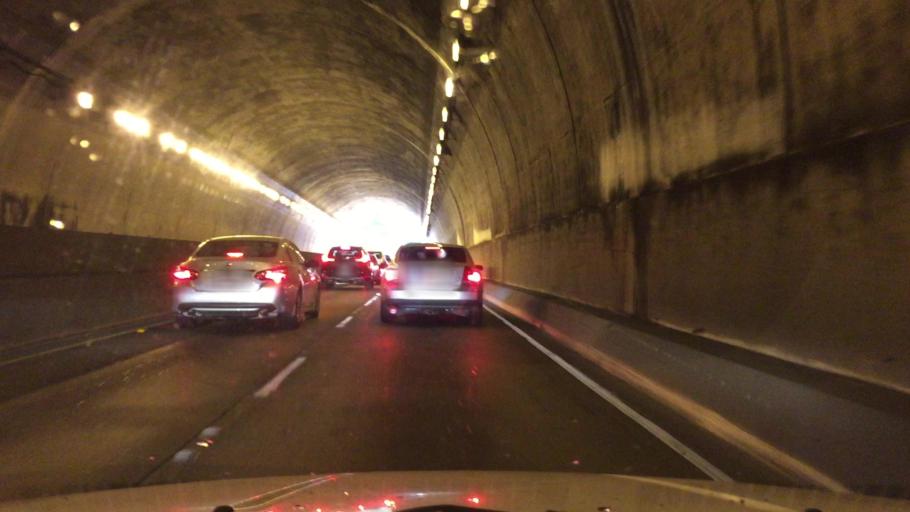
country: US
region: California
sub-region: San Francisco County
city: San Francisco
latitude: 37.7917
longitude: -122.4705
